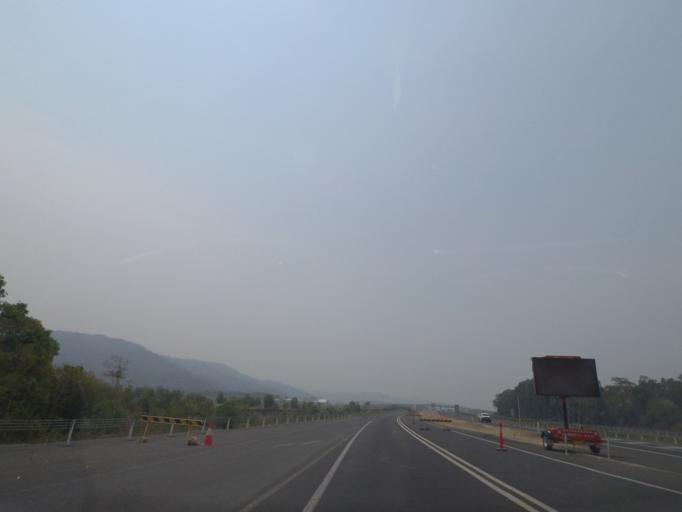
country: AU
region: New South Wales
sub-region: Ballina
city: Ballina
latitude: -28.9079
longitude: 153.4788
